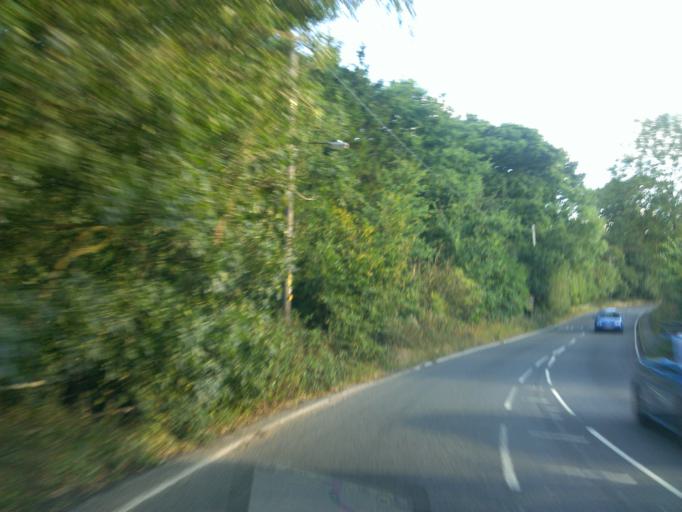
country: GB
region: England
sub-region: Essex
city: Sible Hedingham
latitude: 51.9314
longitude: 0.5960
